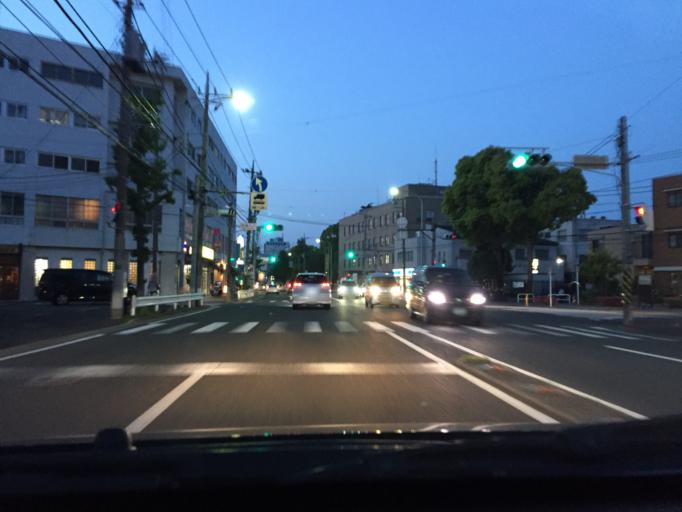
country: JP
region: Kanagawa
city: Yokohama
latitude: 35.4214
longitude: 139.6013
